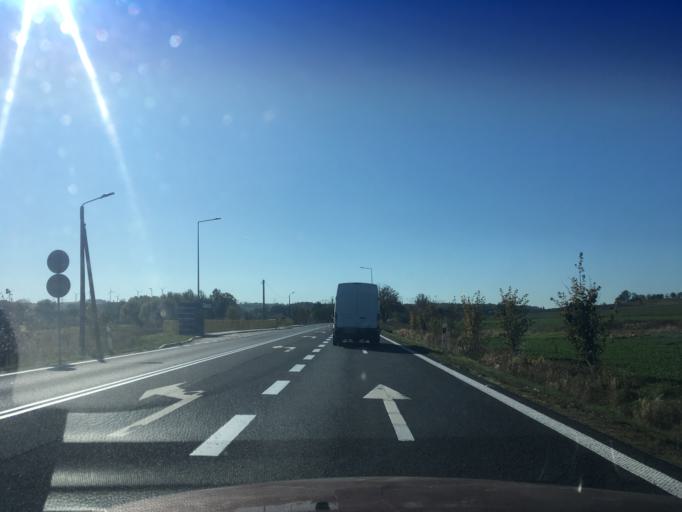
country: DE
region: Saxony
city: Ostritz
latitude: 51.0347
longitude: 14.9721
